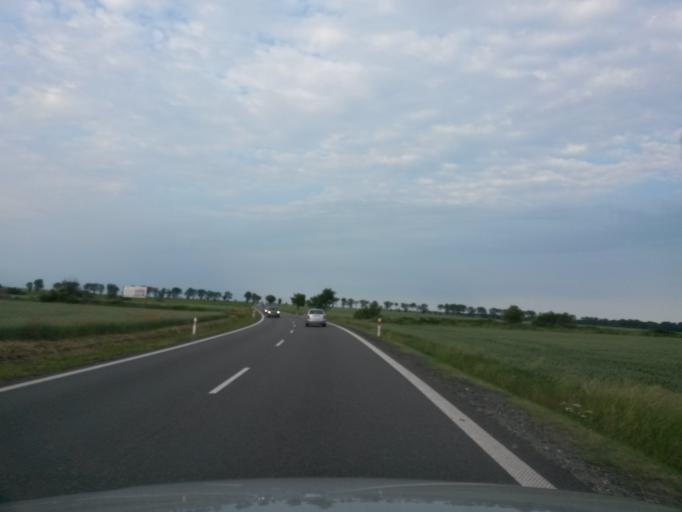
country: PL
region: Lower Silesian Voivodeship
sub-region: Powiat swidnicki
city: Zarow
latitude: 50.9965
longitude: 16.5012
